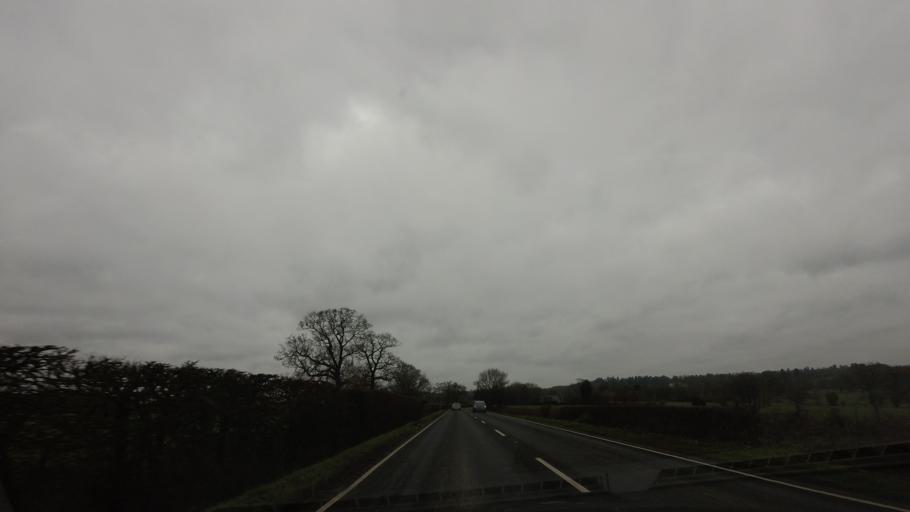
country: GB
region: England
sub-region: Kent
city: Marden
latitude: 51.2102
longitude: 0.5158
